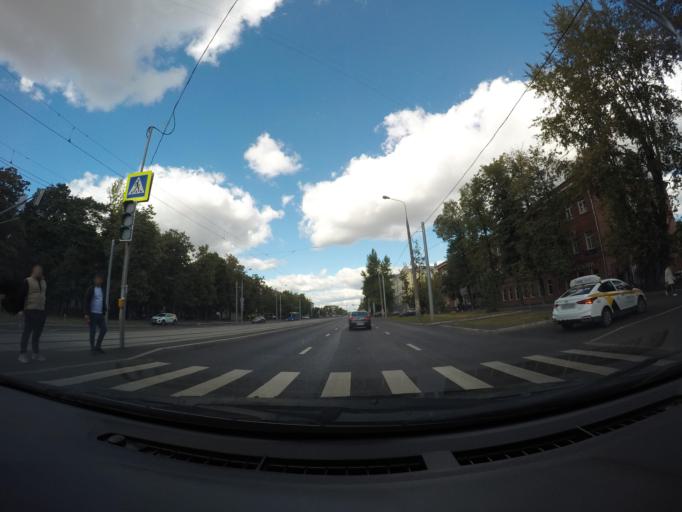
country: RU
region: Moscow
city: Lefortovo
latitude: 55.7656
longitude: 37.7323
